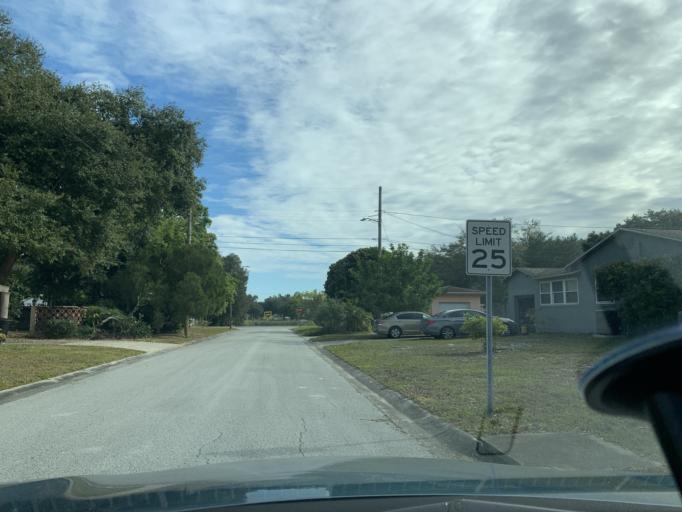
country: US
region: Florida
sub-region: Pinellas County
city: Saint Petersburg
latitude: 27.7947
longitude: -82.6590
